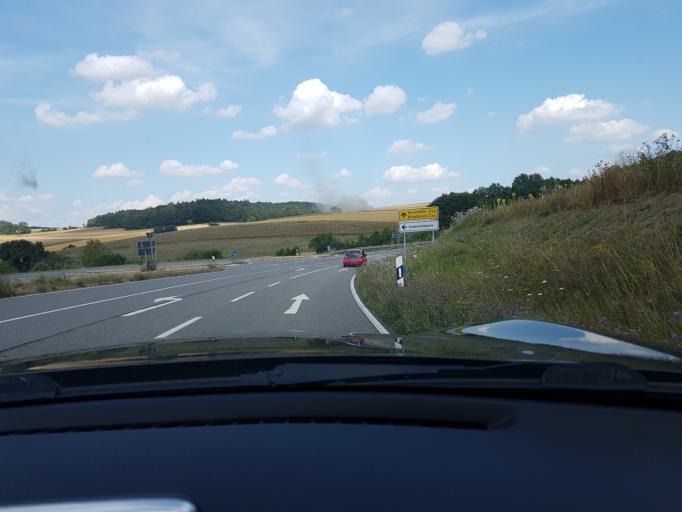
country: DE
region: Baden-Wuerttemberg
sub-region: Karlsruhe Region
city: Billigheim
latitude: 49.3391
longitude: 9.2820
